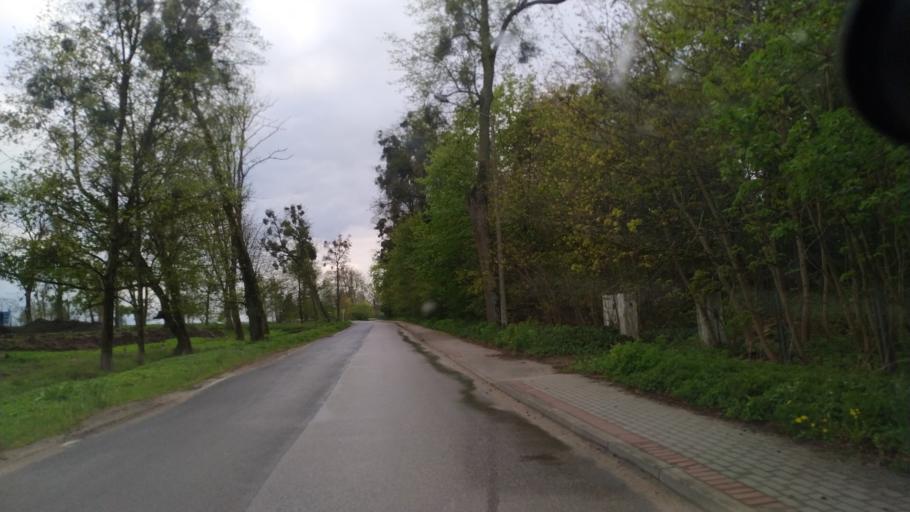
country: PL
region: Pomeranian Voivodeship
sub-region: Powiat starogardzki
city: Smetowo Graniczne
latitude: 53.7352
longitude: 18.6477
